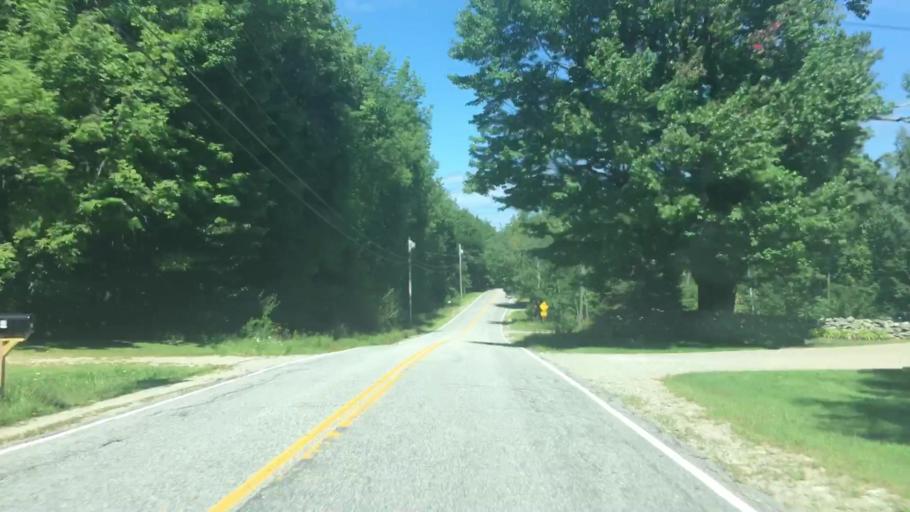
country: US
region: Maine
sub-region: Kennebec County
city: Monmouth
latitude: 44.1743
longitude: -69.9415
